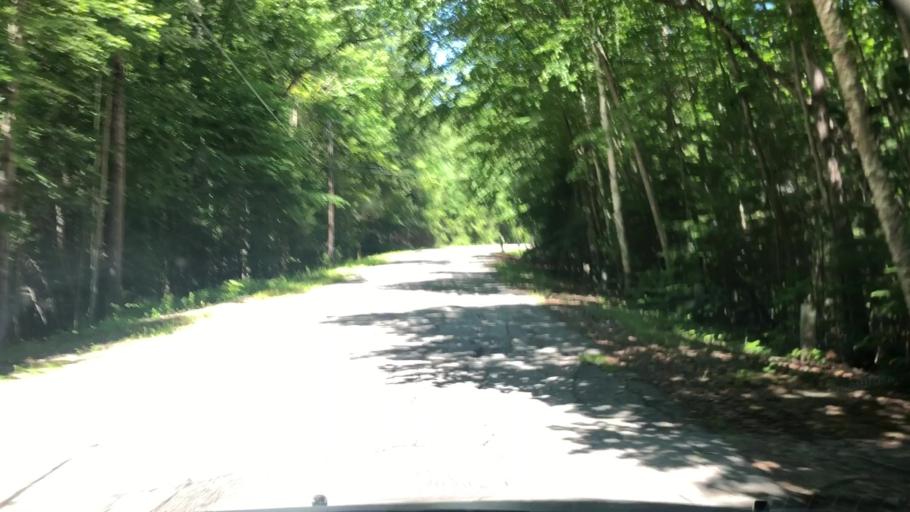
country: US
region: New Hampshire
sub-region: Hillsborough County
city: Mont Vernon
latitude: 42.9016
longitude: -71.6086
